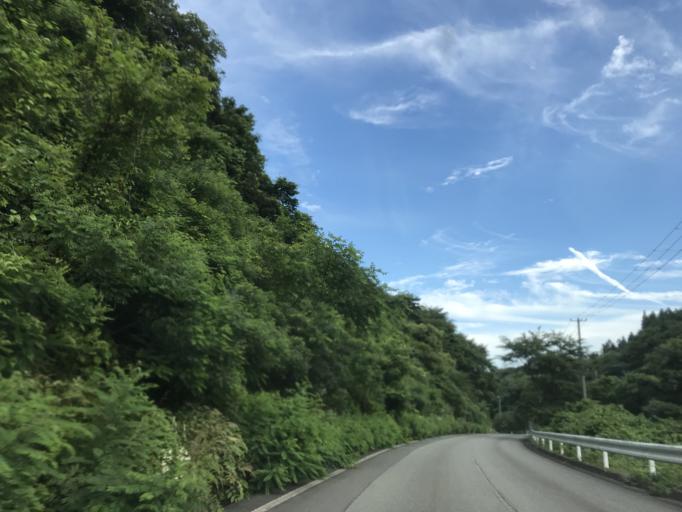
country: JP
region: Iwate
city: Ichinoseki
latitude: 38.8968
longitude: 141.0054
